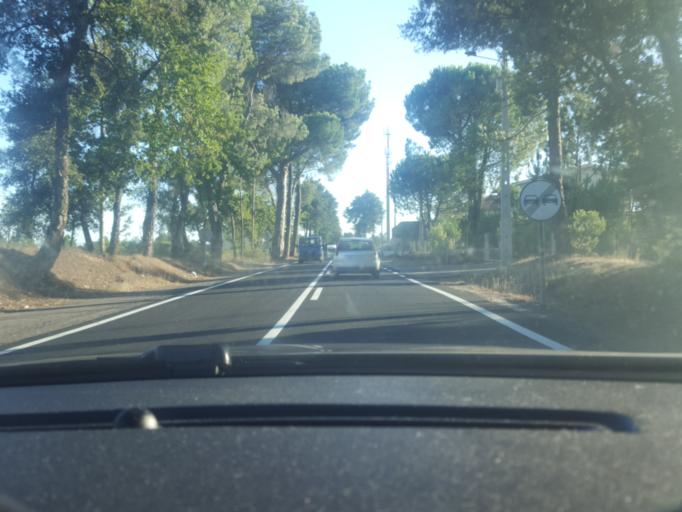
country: PT
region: Viseu
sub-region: Mangualde
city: Mangualde
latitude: 40.5844
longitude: -7.8049
